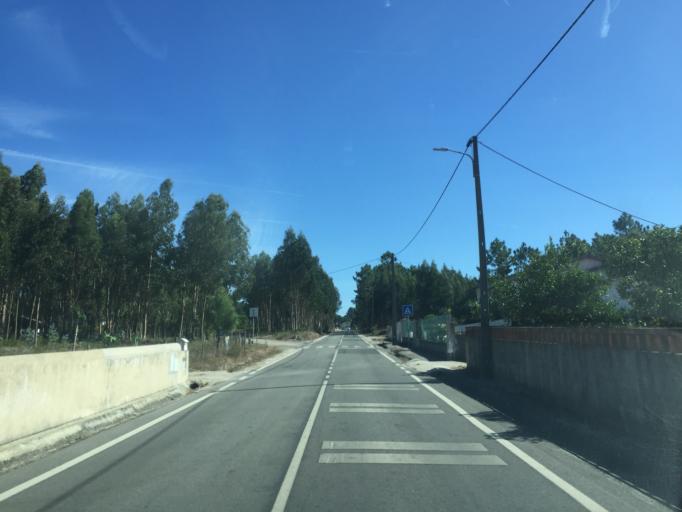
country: PT
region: Coimbra
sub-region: Figueira da Foz
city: Alhadas
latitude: 40.2194
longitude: -8.8161
